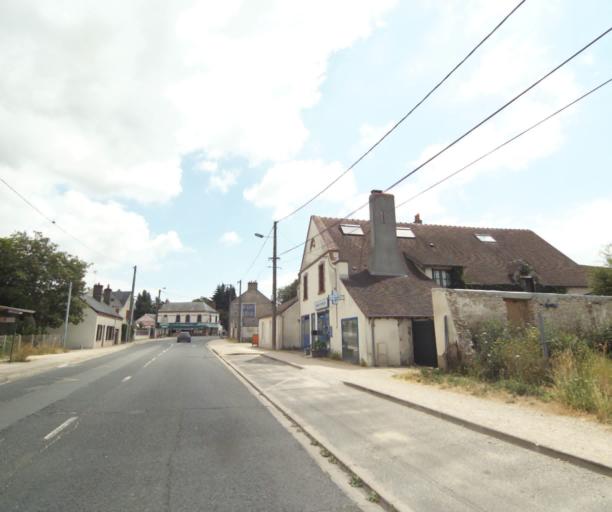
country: FR
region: Centre
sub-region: Departement du Loiret
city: Saint-Jean-de-Braye
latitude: 47.9086
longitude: 1.9750
